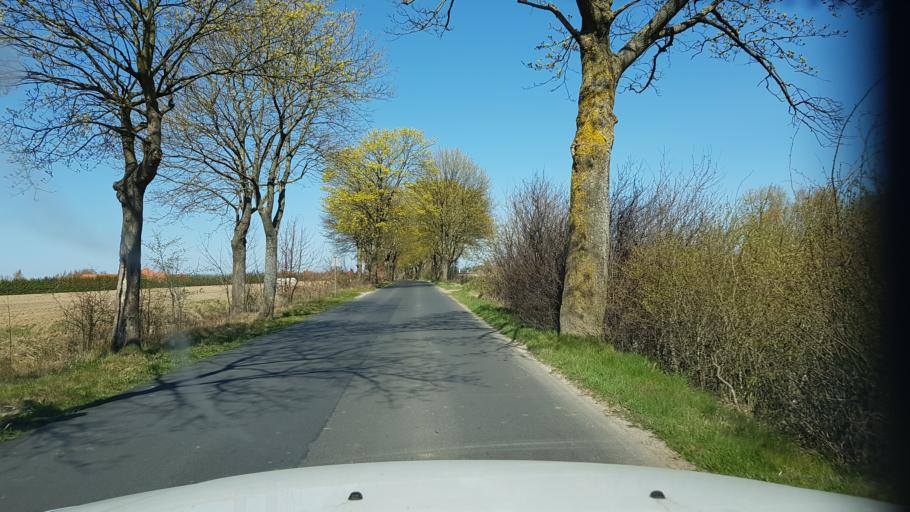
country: PL
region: West Pomeranian Voivodeship
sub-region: Koszalin
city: Koszalin
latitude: 54.2353
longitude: 16.1637
